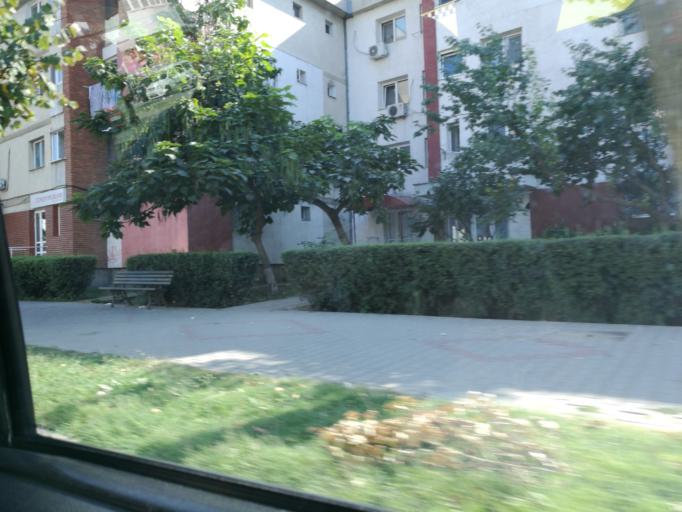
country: RO
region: Iasi
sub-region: Municipiul Iasi
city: Iasi
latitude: 47.1698
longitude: 27.5637
